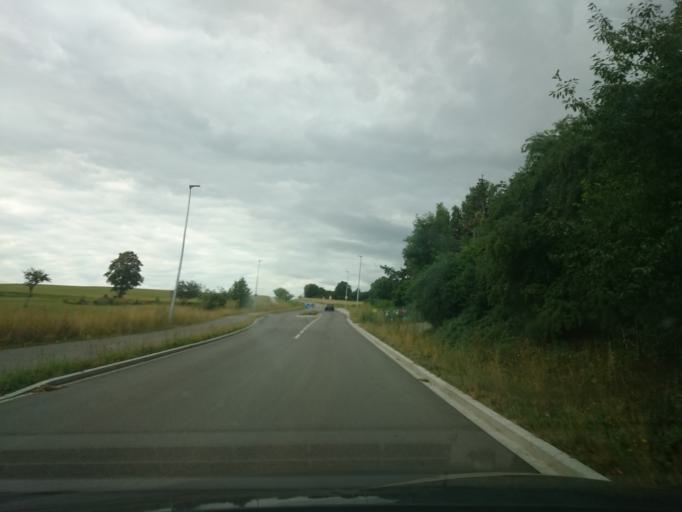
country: DE
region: Bavaria
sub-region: Regierungsbezirk Mittelfranken
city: Hilpoltstein
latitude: 49.1477
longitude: 11.2165
